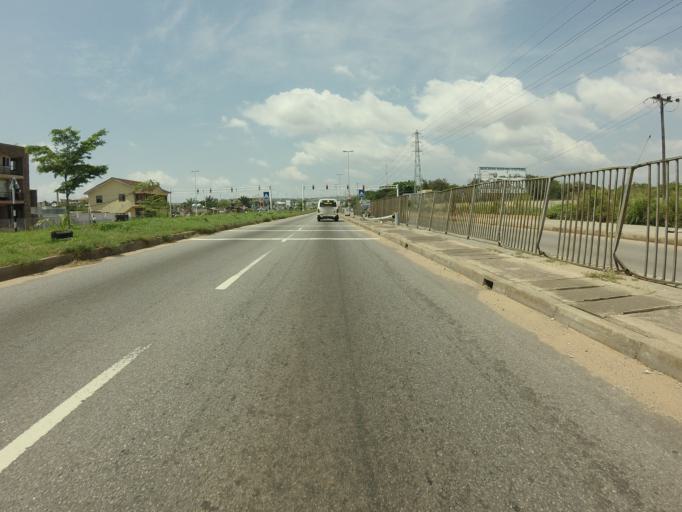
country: GH
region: Greater Accra
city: Gbawe
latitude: 5.5894
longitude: -0.2831
